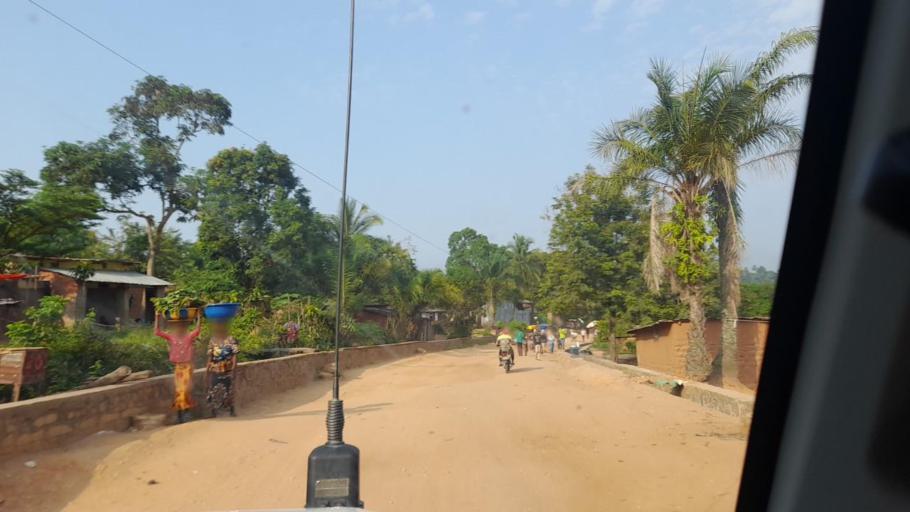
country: CD
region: Kasai-Occidental
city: Kananga
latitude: -5.8944
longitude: 22.3847
